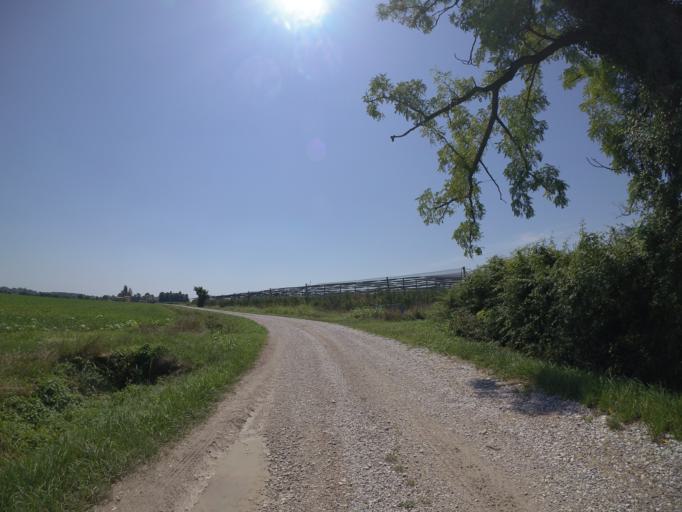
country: IT
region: Friuli Venezia Giulia
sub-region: Provincia di Udine
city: Varmo
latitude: 45.9144
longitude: 13.0024
